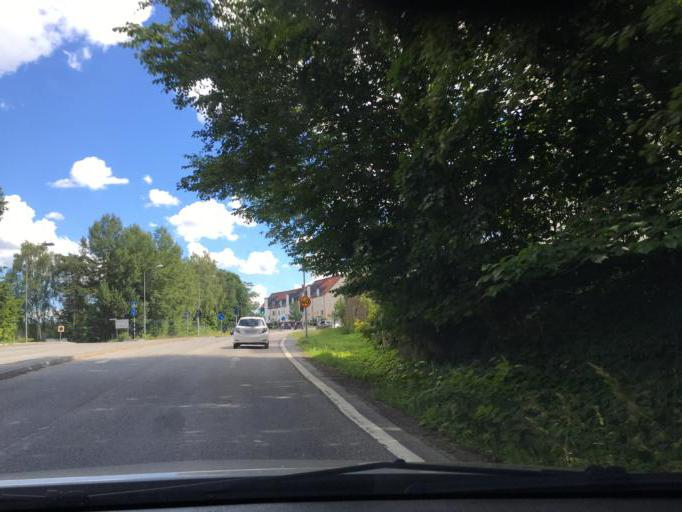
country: SE
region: Stockholm
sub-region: Nacka Kommun
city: Nacka
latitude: 59.3064
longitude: 18.1469
